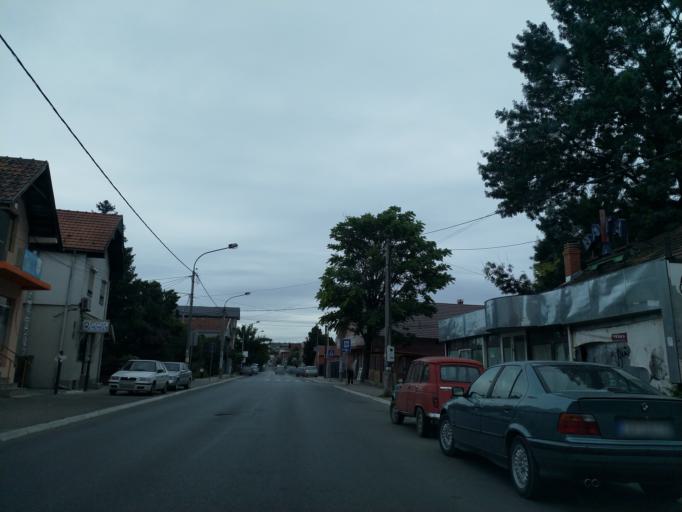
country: RS
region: Central Serbia
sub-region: Pomoravski Okrug
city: Jagodina
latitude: 43.9852
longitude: 21.2508
